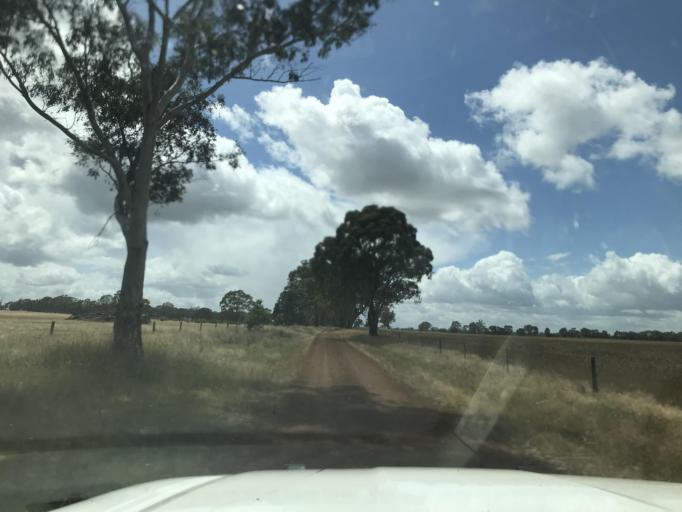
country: AU
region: South Australia
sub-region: Wattle Range
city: Penola
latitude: -37.1819
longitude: 141.4474
